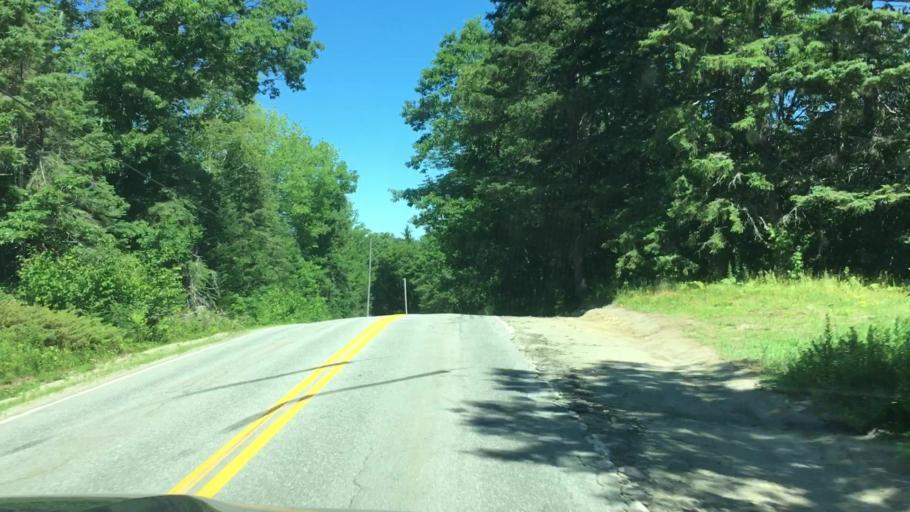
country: US
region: Maine
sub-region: Hancock County
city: Penobscot
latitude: 44.4223
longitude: -68.7061
